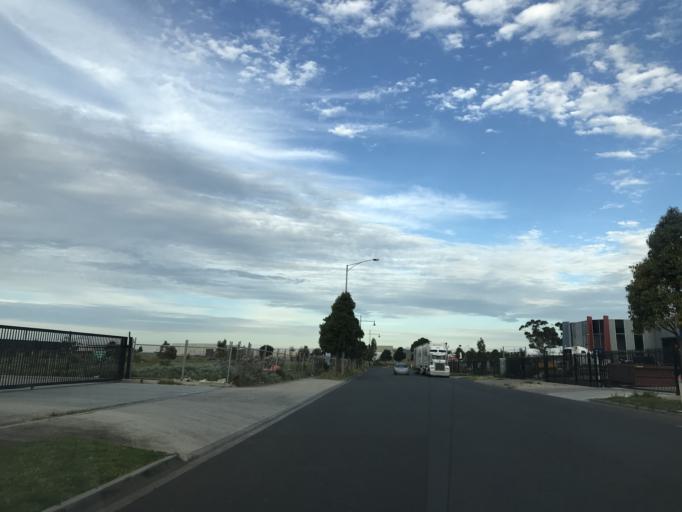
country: AU
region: Victoria
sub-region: Wyndham
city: Truganina
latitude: -37.8035
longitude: 144.7574
